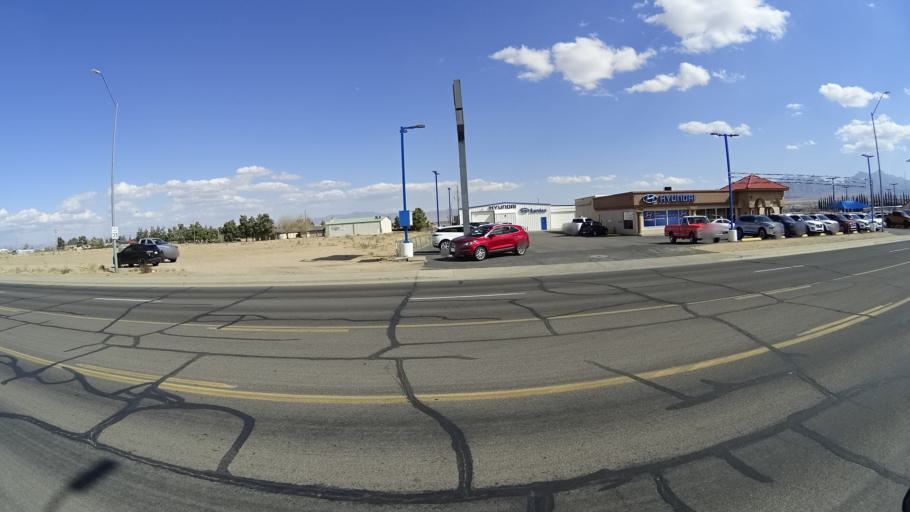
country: US
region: Arizona
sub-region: Mohave County
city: New Kingman-Butler
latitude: 35.2448
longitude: -114.0385
